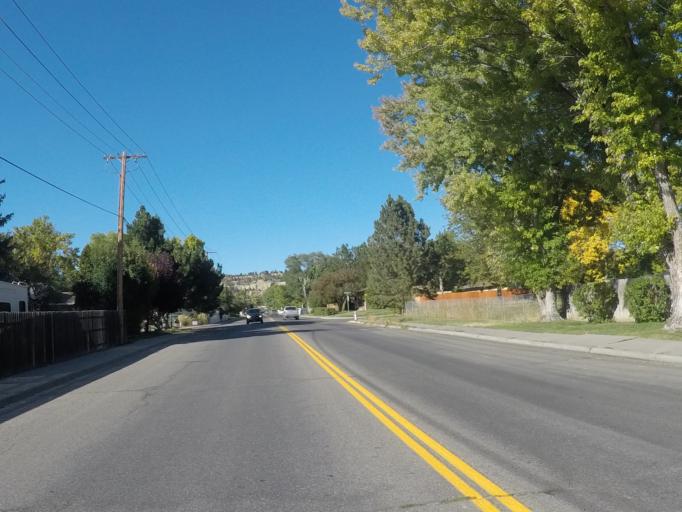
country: US
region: Montana
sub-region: Yellowstone County
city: Billings
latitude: 45.7892
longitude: -108.5904
